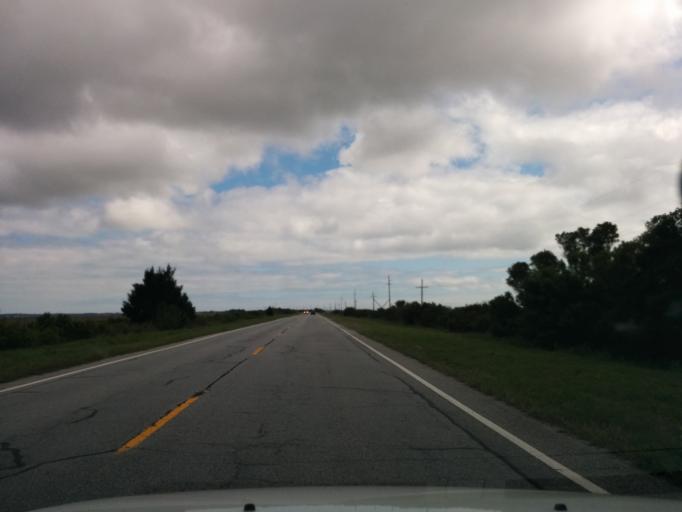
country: US
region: Georgia
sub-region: Glynn County
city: Brunswick
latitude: 31.0847
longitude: -81.4765
